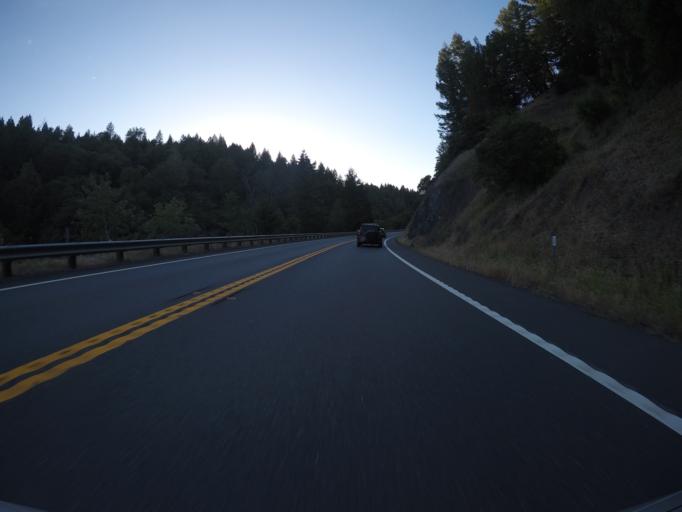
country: US
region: California
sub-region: Mendocino County
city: Laytonville
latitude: 39.7630
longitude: -123.5422
